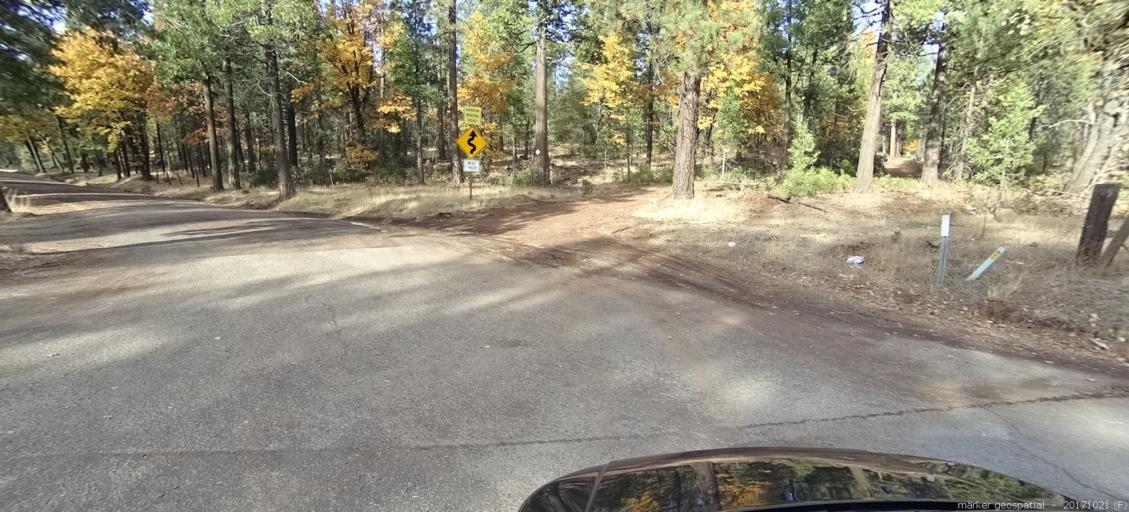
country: US
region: California
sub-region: Shasta County
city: Burney
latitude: 40.8726
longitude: -121.6946
